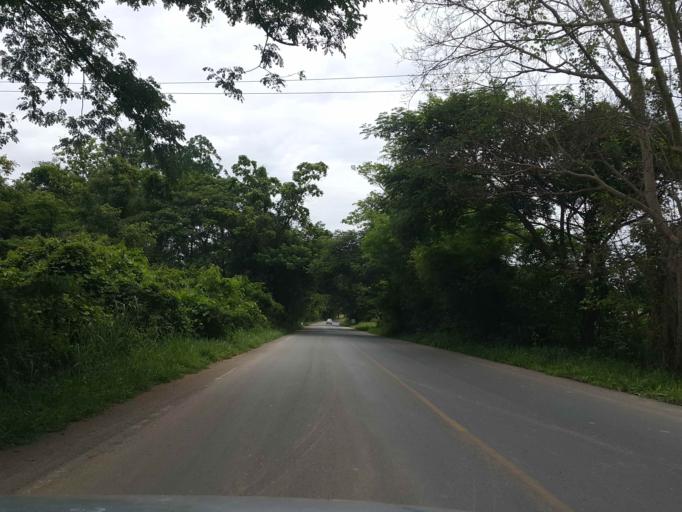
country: TH
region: Lampang
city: Thoen
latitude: 17.5669
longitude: 99.3305
